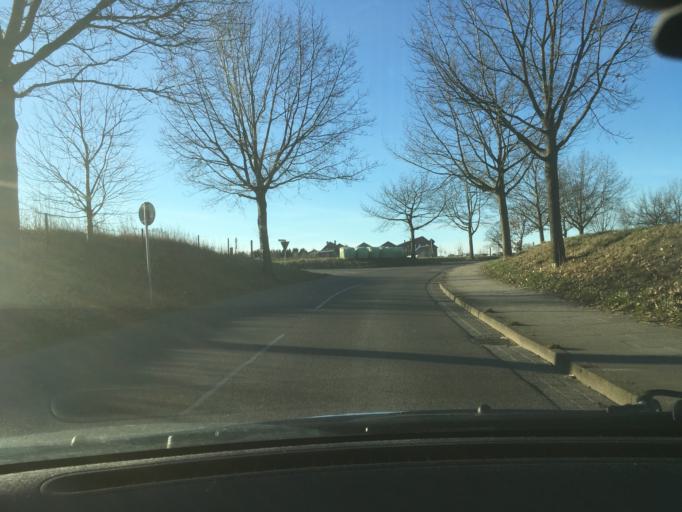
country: DE
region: Lower Saxony
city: Seevetal
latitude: 53.4011
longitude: 9.9699
